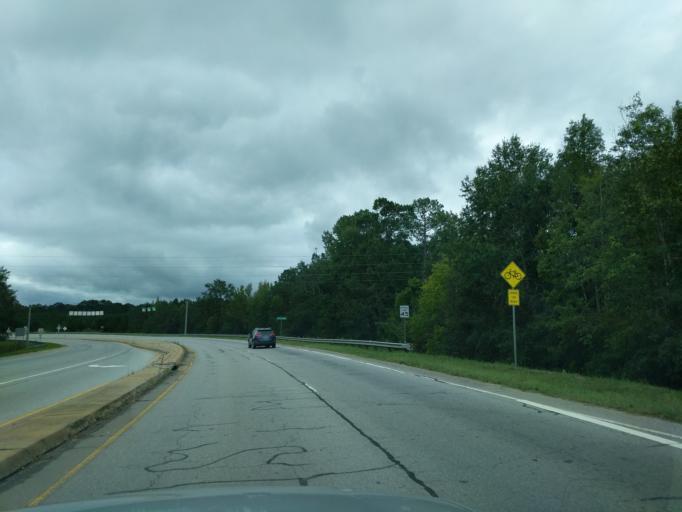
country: US
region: Georgia
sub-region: Wilkes County
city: Washington
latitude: 33.7260
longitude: -82.7150
